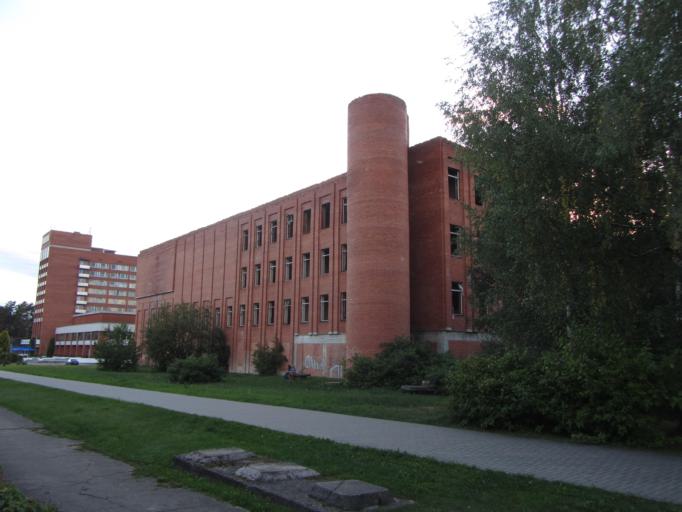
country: LT
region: Utenos apskritis
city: Visaginas
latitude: 55.5996
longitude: 26.4368
